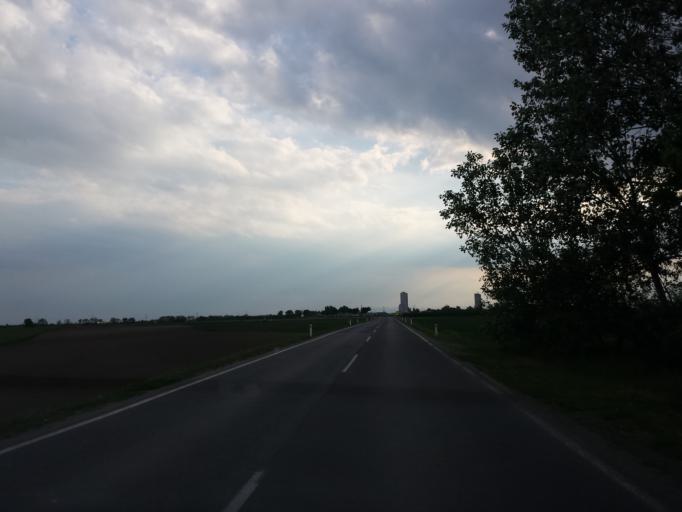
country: AT
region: Lower Austria
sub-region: Politischer Bezirk Ganserndorf
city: Grosshofen
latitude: 48.2476
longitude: 16.6023
